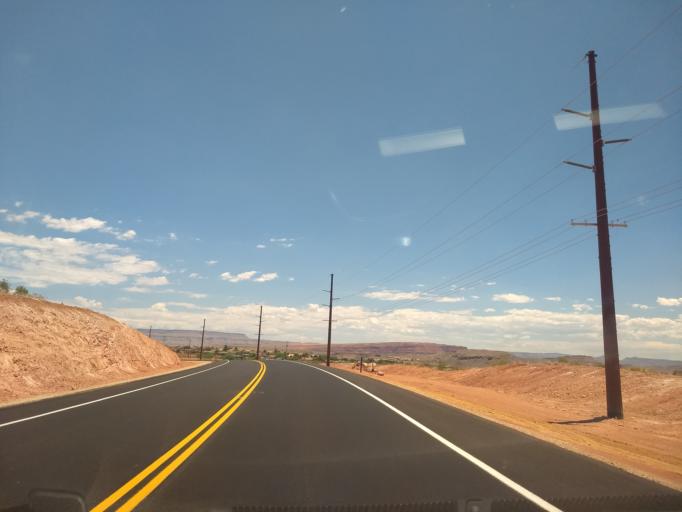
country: US
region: Utah
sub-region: Washington County
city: Washington
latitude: 37.1492
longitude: -113.5151
